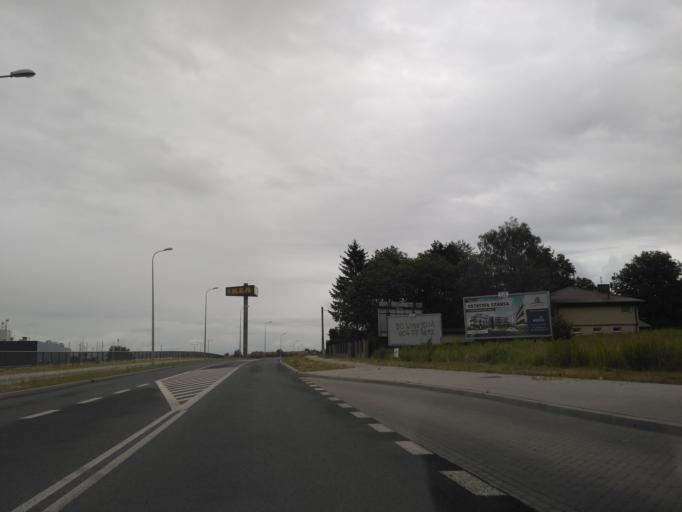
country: PL
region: Lublin Voivodeship
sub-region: Powiat lubelski
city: Lublin
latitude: 51.2808
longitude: 22.5702
